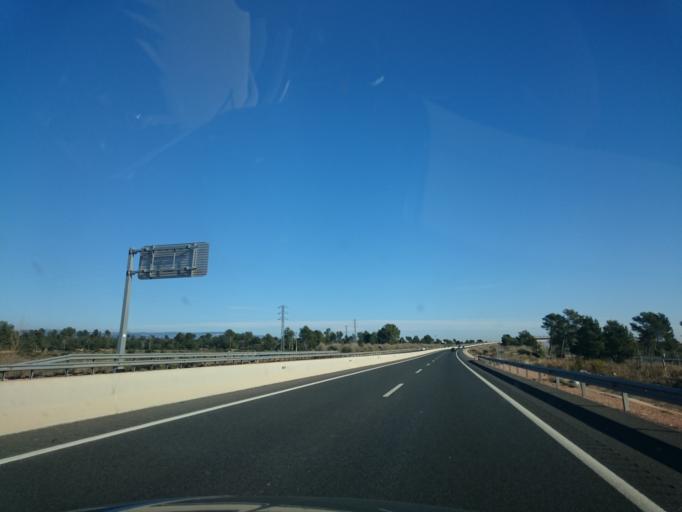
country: ES
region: Catalonia
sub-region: Provincia de Tarragona
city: Vilanova d'Escornalbou
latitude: 41.0328
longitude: 0.9408
